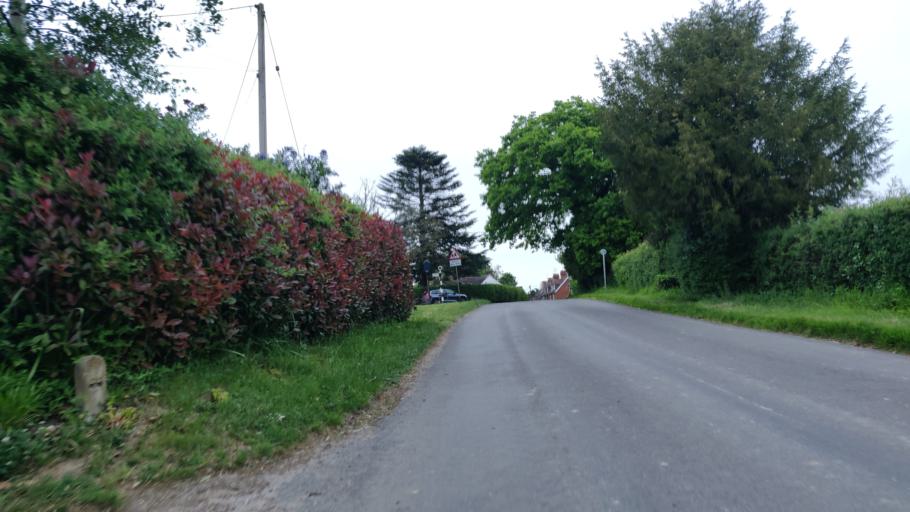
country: GB
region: England
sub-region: West Sussex
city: Southwater
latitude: 51.0074
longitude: -0.3072
